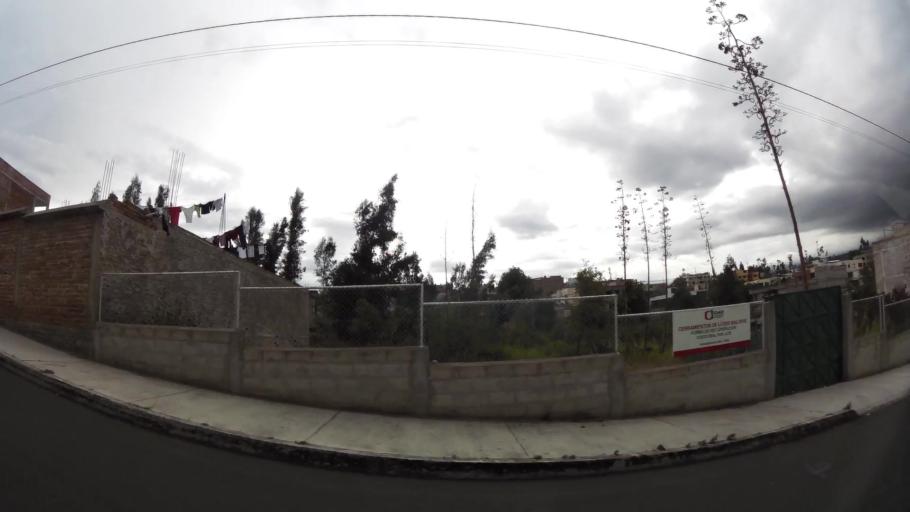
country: EC
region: Tungurahua
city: Ambato
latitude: -1.2670
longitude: -78.6207
